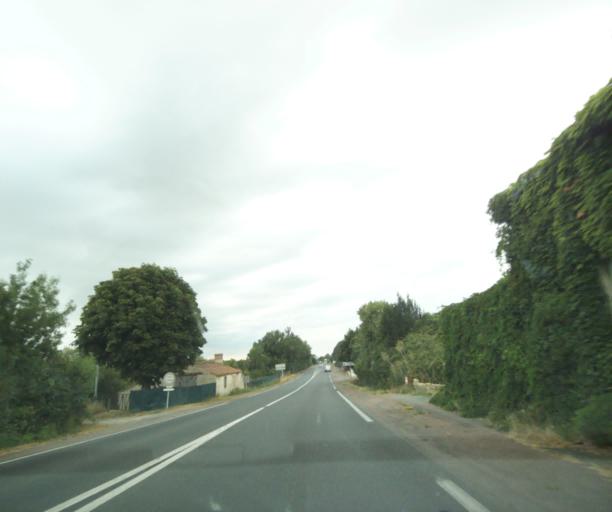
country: FR
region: Pays de la Loire
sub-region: Departement de la Vendee
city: Chaille-les-Marais
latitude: 46.4015
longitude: -1.0330
